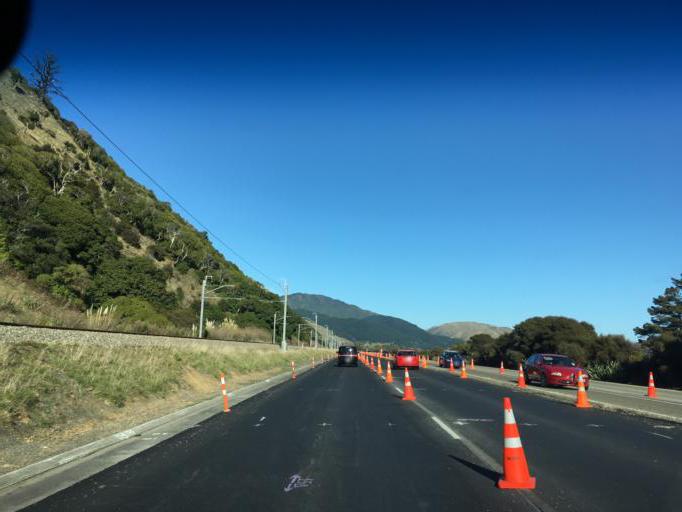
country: NZ
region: Wellington
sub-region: Kapiti Coast District
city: Paraparaumu
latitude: -40.9469
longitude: 174.9906
